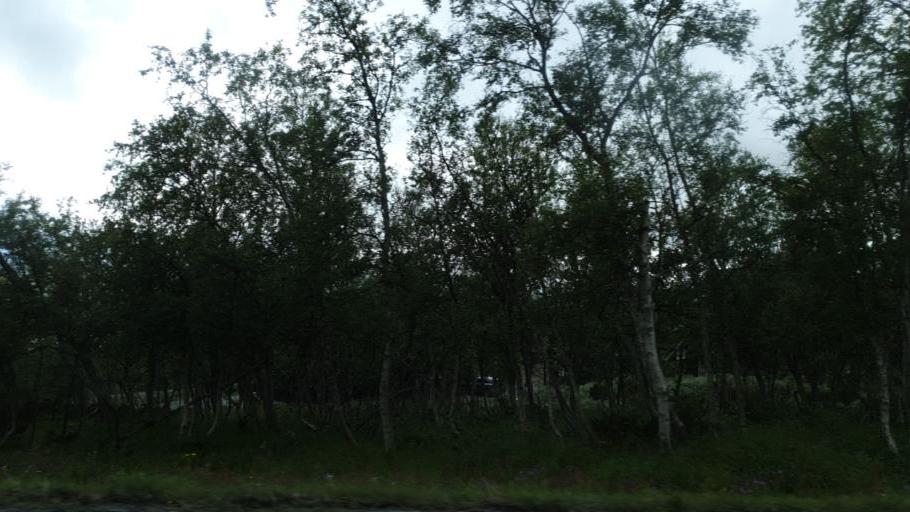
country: NO
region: Oppland
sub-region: Vestre Slidre
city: Slidre
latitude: 61.2649
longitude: 8.8681
